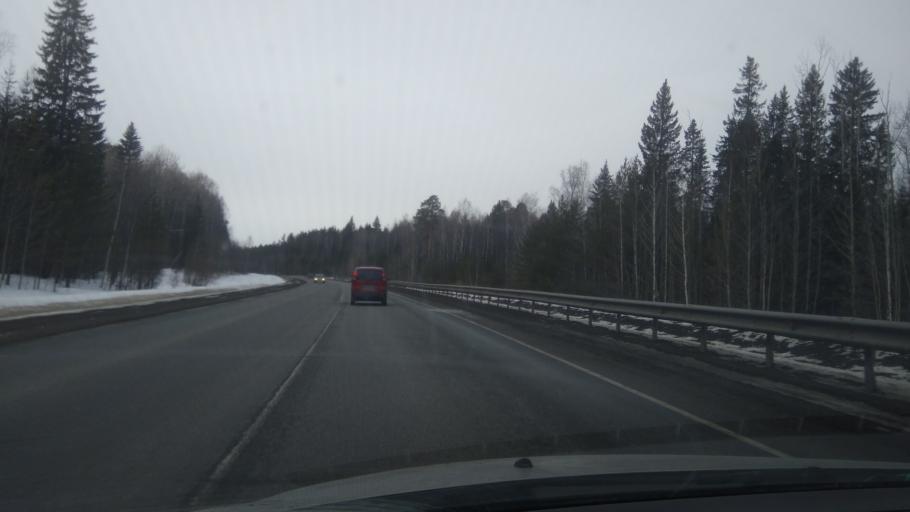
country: RU
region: Sverdlovsk
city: Achit
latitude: 56.7816
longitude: 57.9722
